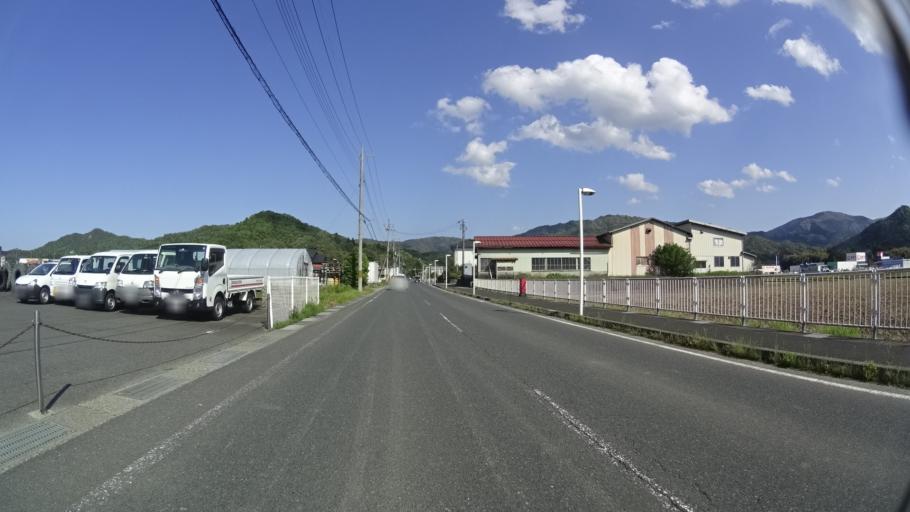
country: JP
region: Kyoto
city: Miyazu
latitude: 35.5325
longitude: 135.1192
